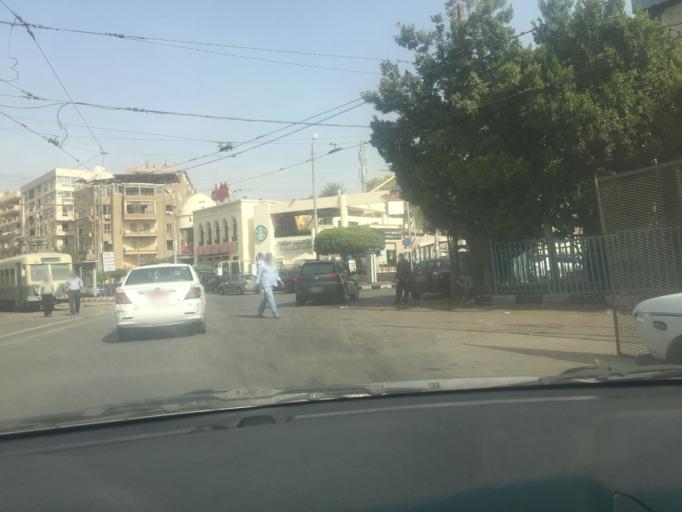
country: EG
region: Muhafazat al Qahirah
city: Cairo
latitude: 30.0853
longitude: 31.3478
